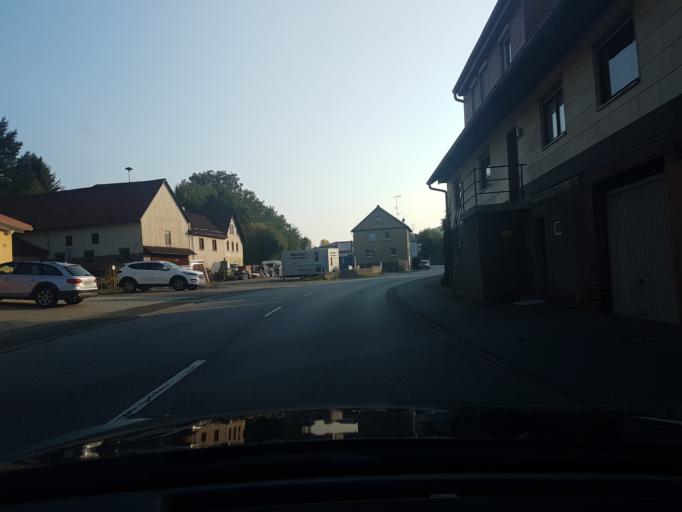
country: DE
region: Hesse
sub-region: Regierungsbezirk Darmstadt
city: Beerfelden
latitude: 49.5939
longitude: 8.9893
